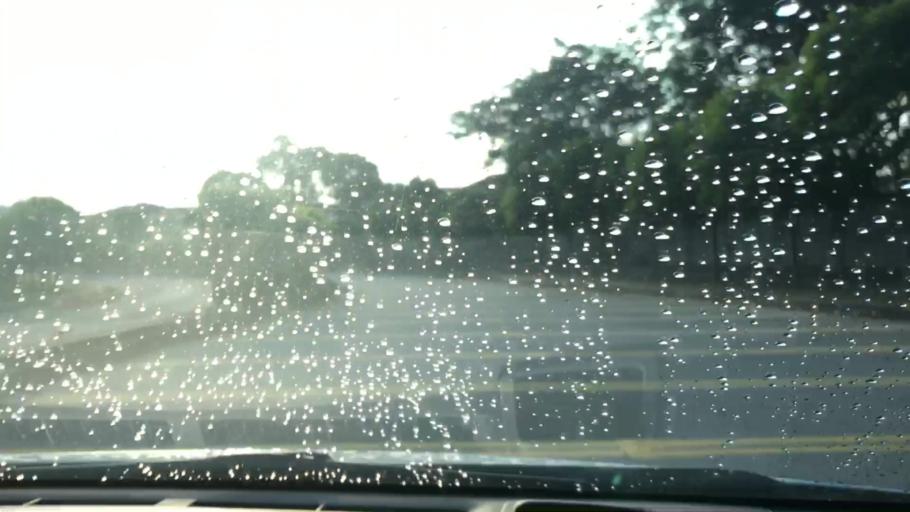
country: MY
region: Putrajaya
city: Putrajaya
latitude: 2.9871
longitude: 101.6671
